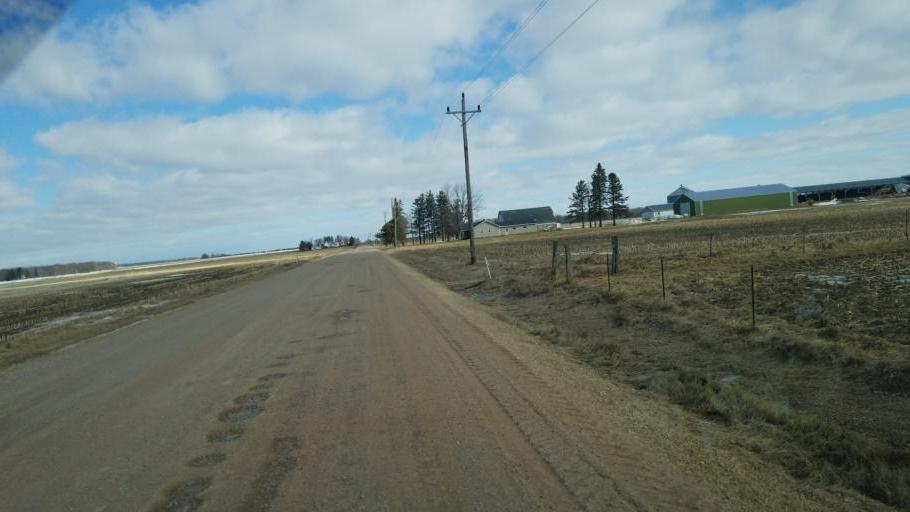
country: US
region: Wisconsin
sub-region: Clark County
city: Loyal
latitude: 44.6722
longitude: -90.4356
